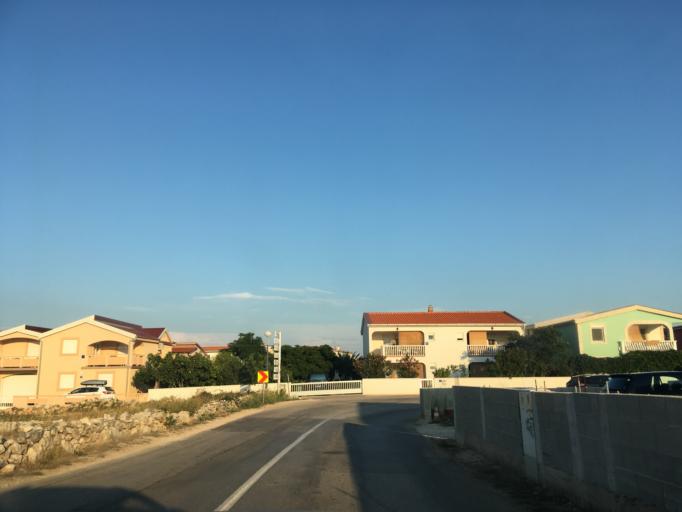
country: HR
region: Zadarska
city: Vir
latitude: 44.2970
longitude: 15.1171
